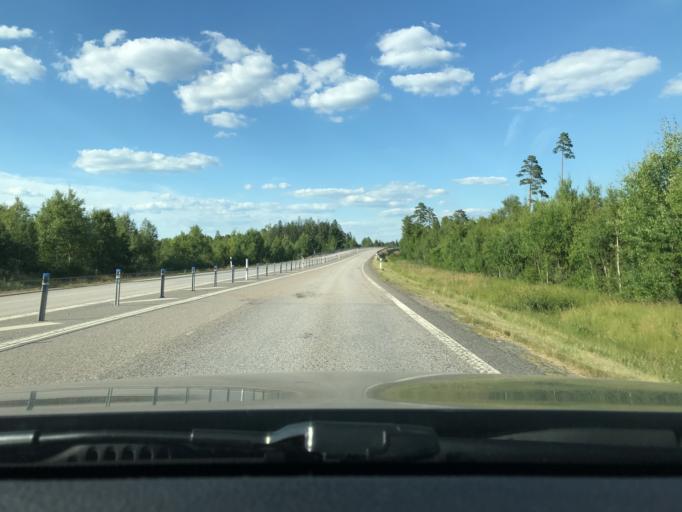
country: SE
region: Kronoberg
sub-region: Alvesta Kommun
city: Vislanda
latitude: 56.7448
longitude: 14.5104
